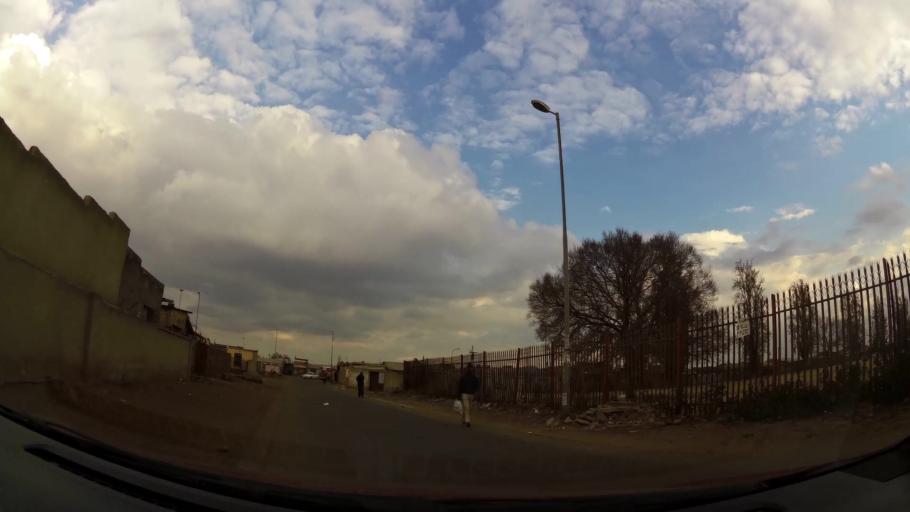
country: ZA
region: Gauteng
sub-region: City of Johannesburg Metropolitan Municipality
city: Soweto
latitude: -26.2413
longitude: 27.8258
